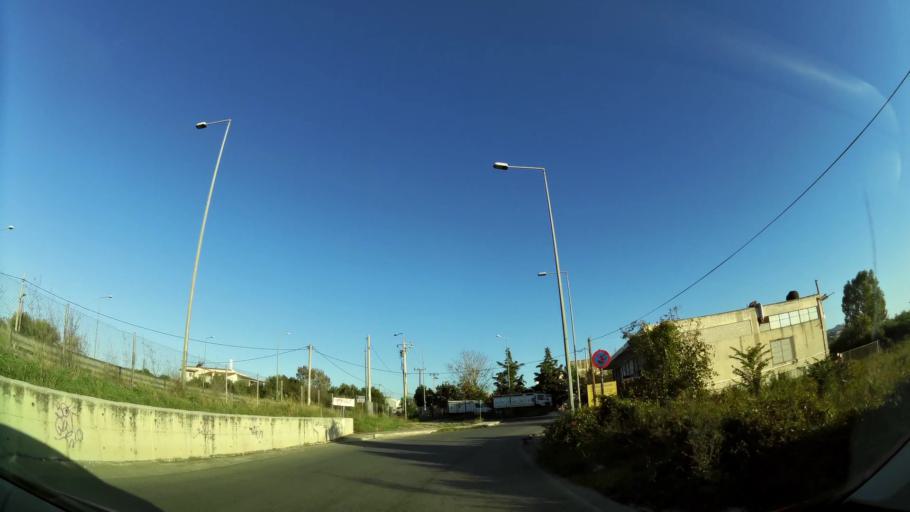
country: GR
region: Attica
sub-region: Nomarchia Anatolikis Attikis
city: Pallini
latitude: 37.9962
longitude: 23.8808
